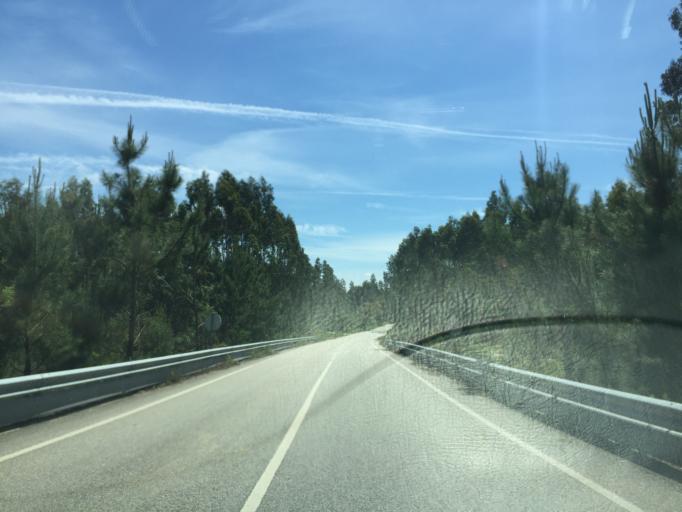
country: PT
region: Coimbra
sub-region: Figueira da Foz
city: Lavos
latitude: 40.0747
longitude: -8.7745
